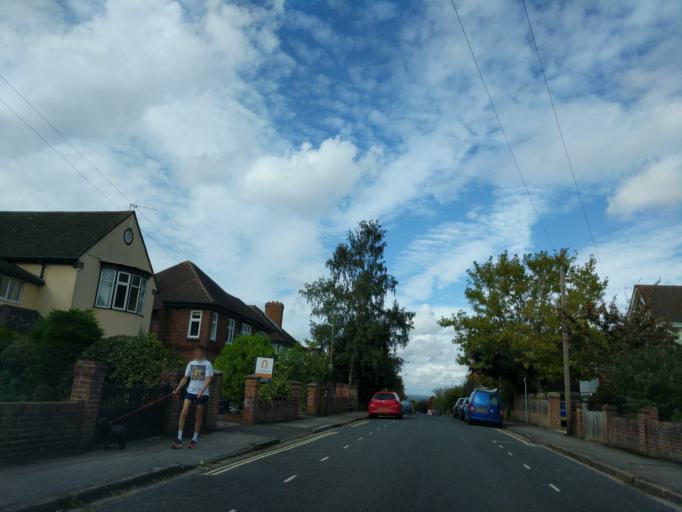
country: GB
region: England
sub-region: Oxfordshire
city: Cowley
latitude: 51.7616
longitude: -1.2201
